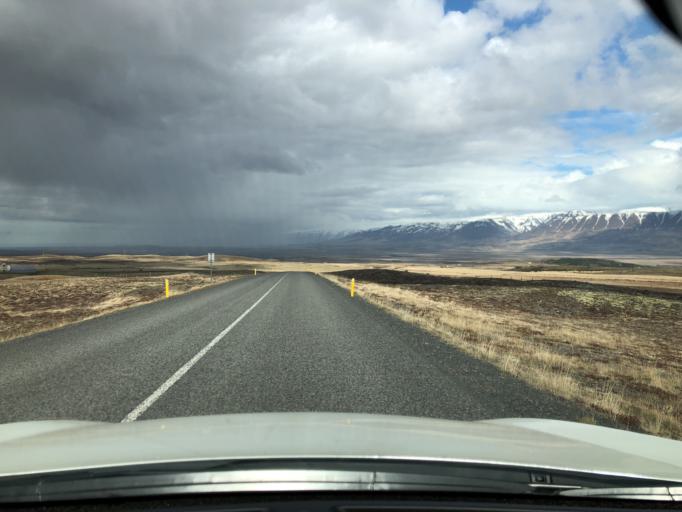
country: IS
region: Northwest
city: Saudarkrokur
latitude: 65.5323
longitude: -19.5129
